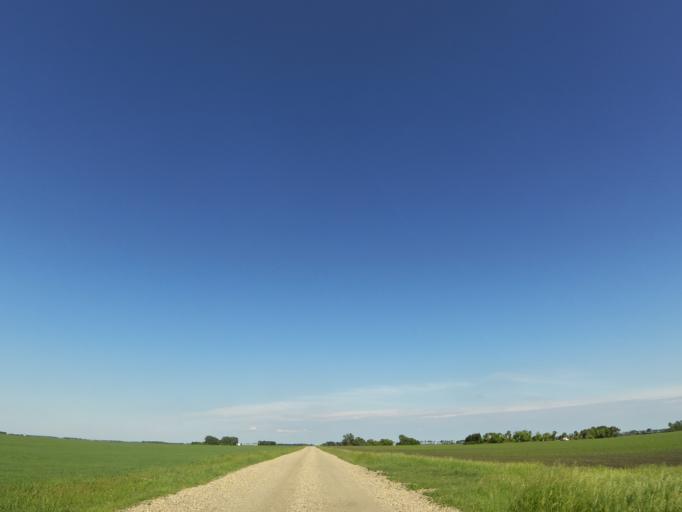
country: US
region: North Dakota
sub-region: Walsh County
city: Grafton
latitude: 48.3534
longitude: -97.2441
